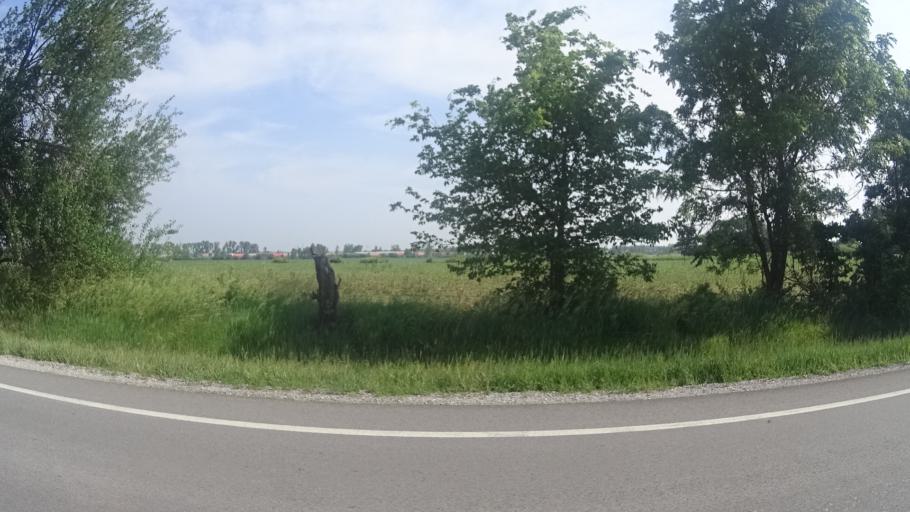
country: US
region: Ohio
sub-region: Huron County
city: Monroeville
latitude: 41.2921
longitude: -82.7607
